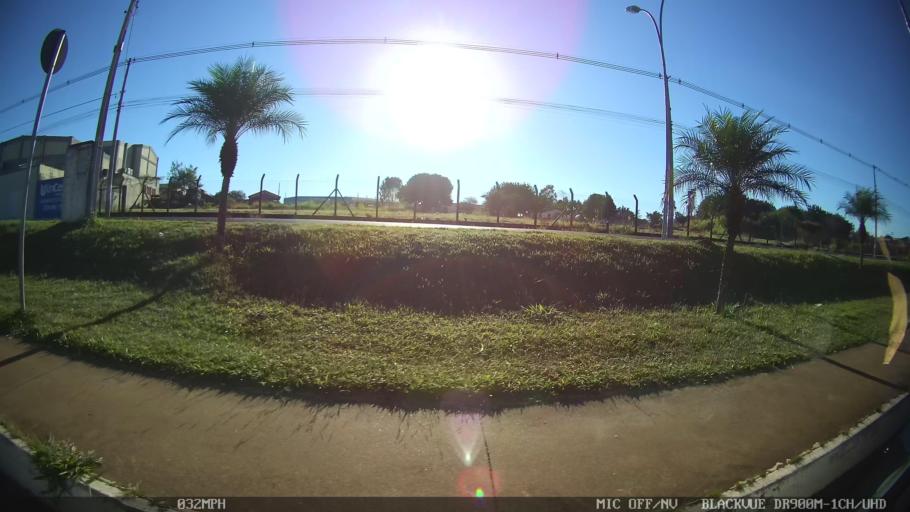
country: BR
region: Sao Paulo
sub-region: Franca
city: Franca
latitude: -20.5768
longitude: -47.3873
